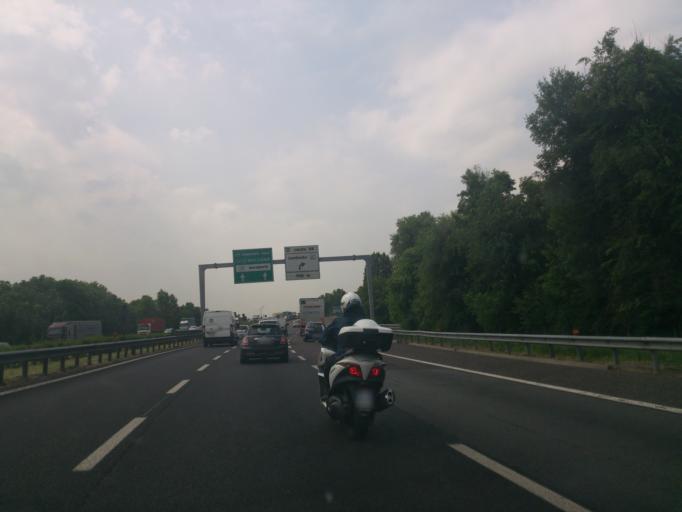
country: IT
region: Lombardy
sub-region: Citta metropolitana di Milano
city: Vimodrone
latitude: 45.4962
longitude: 9.2547
